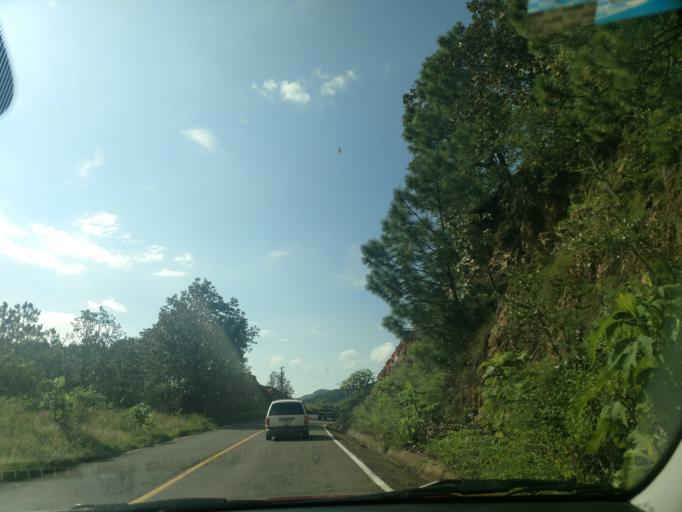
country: MX
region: Jalisco
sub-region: Atengo
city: Soyatlan del Oro
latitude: 20.4879
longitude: -104.3621
